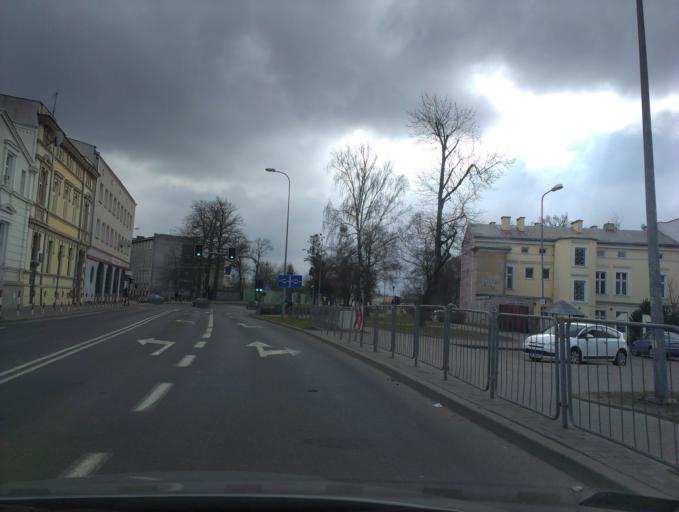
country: PL
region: West Pomeranian Voivodeship
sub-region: Koszalin
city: Koszalin
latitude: 54.1911
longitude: 16.1942
